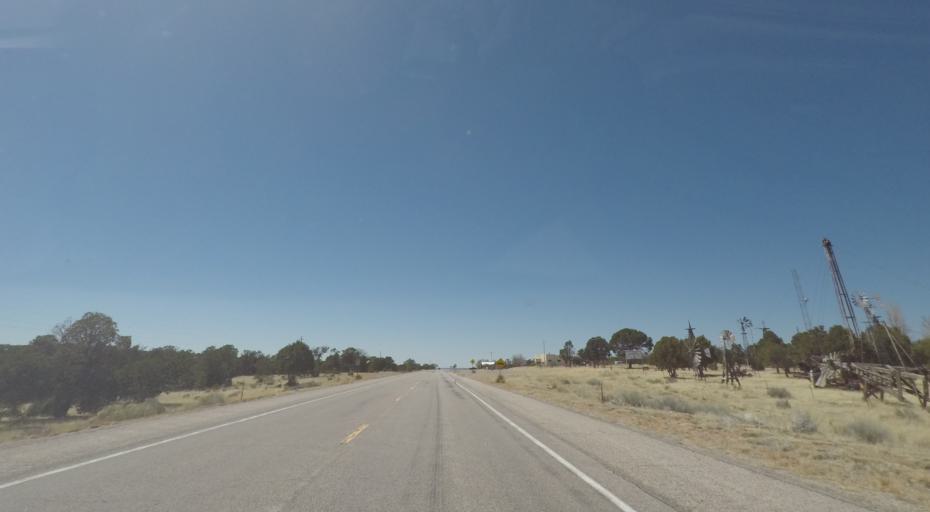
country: US
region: New Mexico
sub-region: Socorro County
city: Alamo
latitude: 34.2977
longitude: -108.1264
